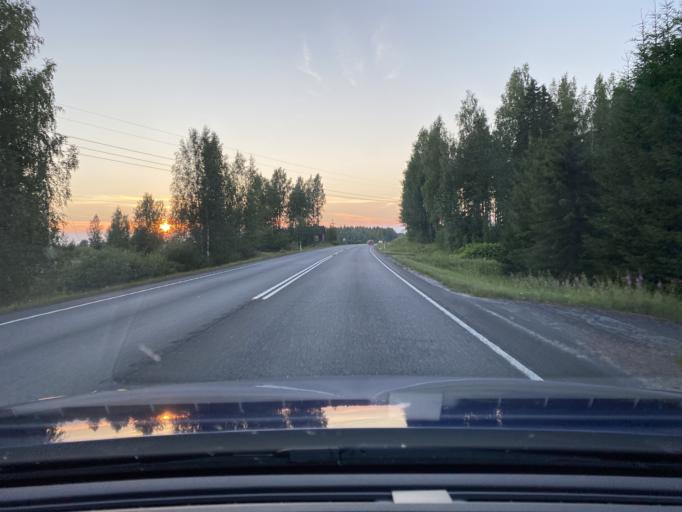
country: FI
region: Pirkanmaa
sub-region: Luoteis-Pirkanmaa
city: Ikaalinen
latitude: 61.8199
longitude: 22.9507
